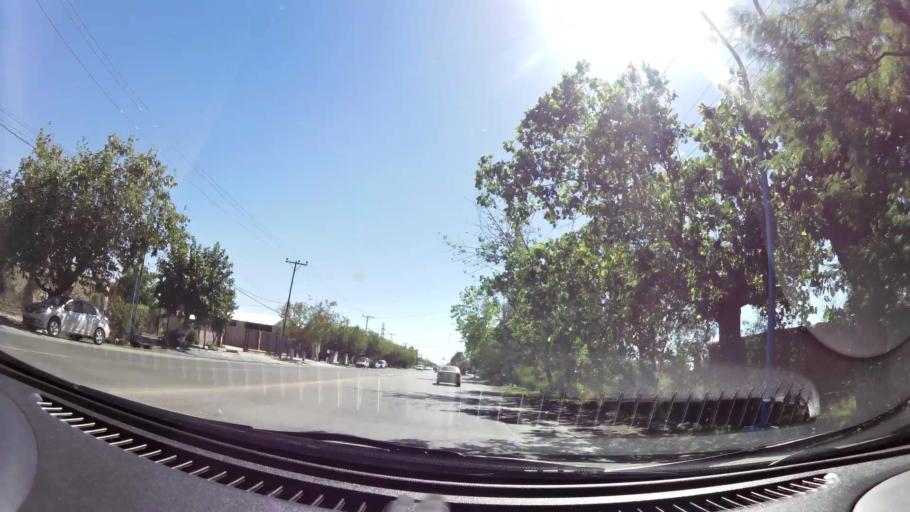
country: AR
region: San Juan
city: Villa Krause
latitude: -31.5959
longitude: -68.5400
